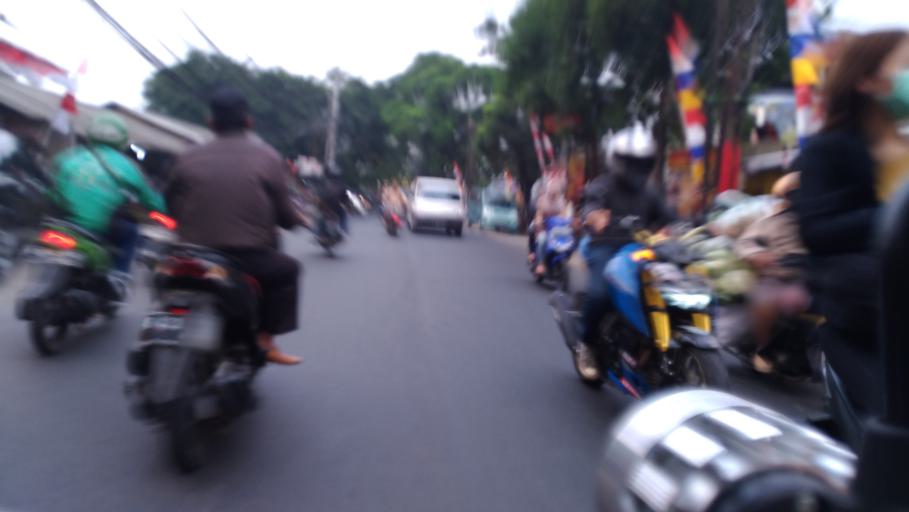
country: ID
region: West Java
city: Depok
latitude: -6.3490
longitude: 106.8768
